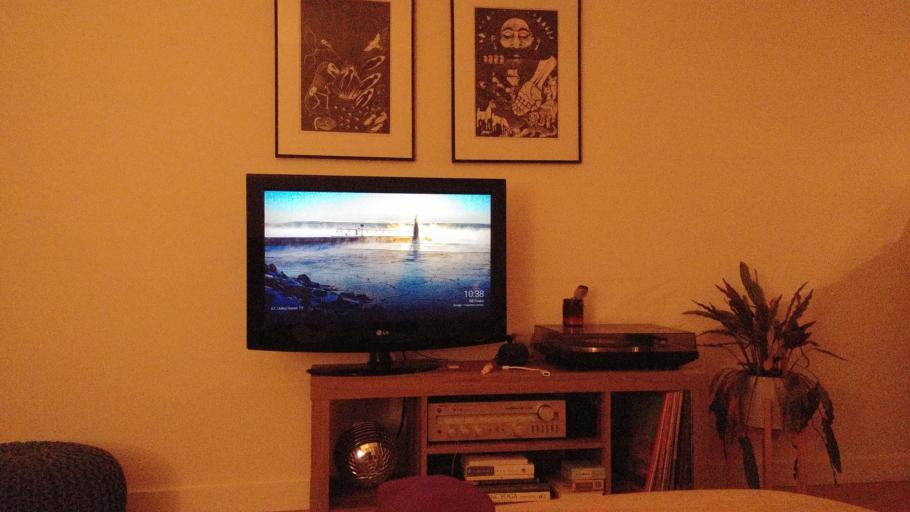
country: CA
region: British Columbia
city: Victoria
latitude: 48.4436
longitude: -123.3884
